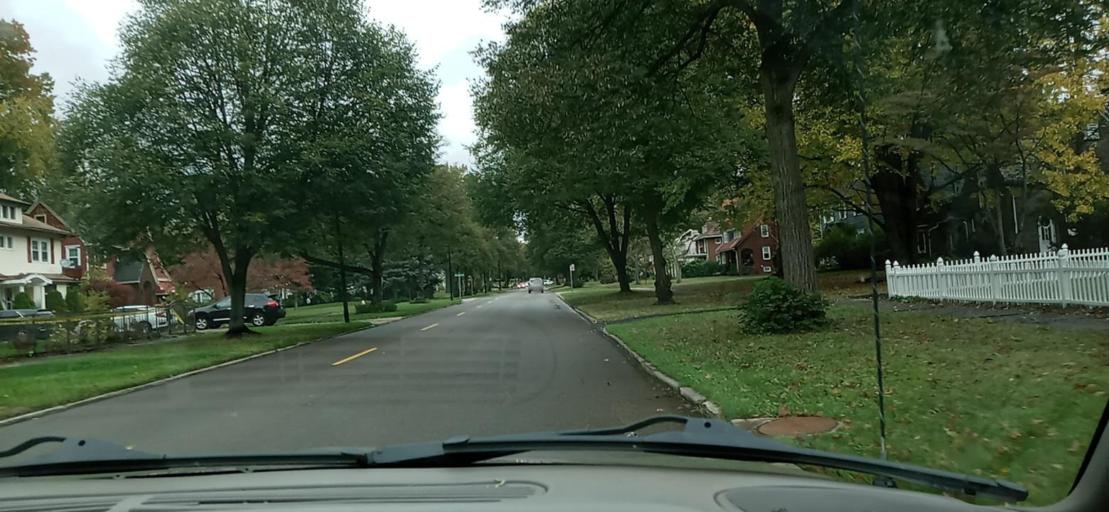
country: US
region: Ohio
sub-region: Summit County
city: Akron
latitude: 41.0924
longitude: -81.5682
